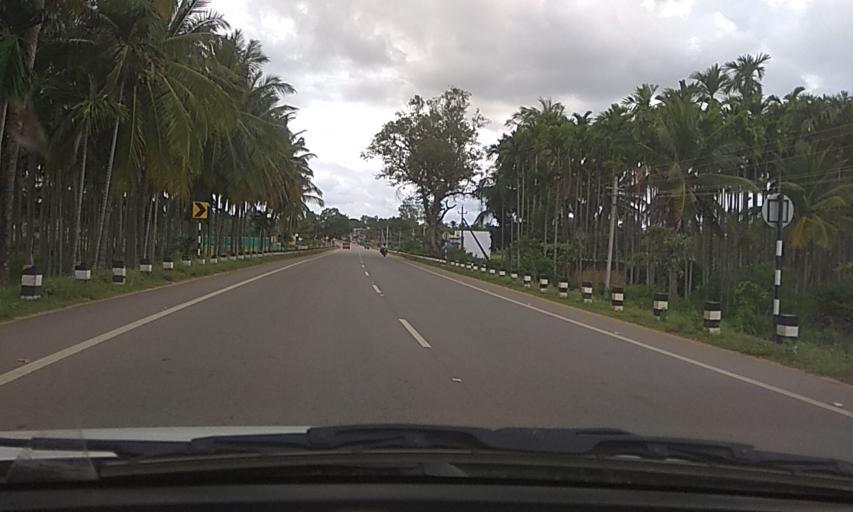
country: IN
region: Karnataka
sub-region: Tumkur
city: Tumkur
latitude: 13.2989
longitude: 77.0925
